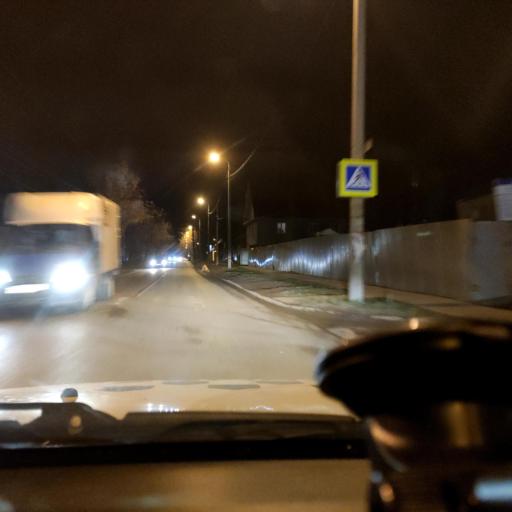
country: RU
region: Perm
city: Perm
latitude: 58.0307
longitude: 56.3276
